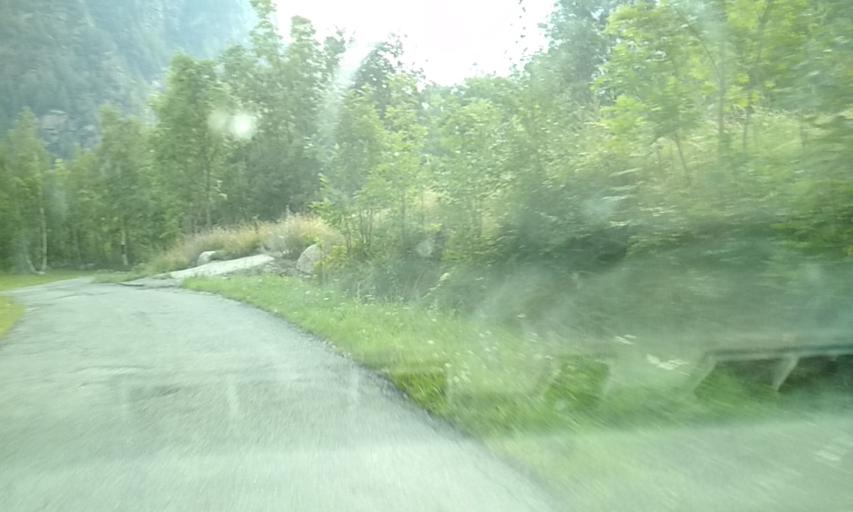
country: IT
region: Piedmont
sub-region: Provincia di Torino
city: Noasca
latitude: 45.4560
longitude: 7.3037
